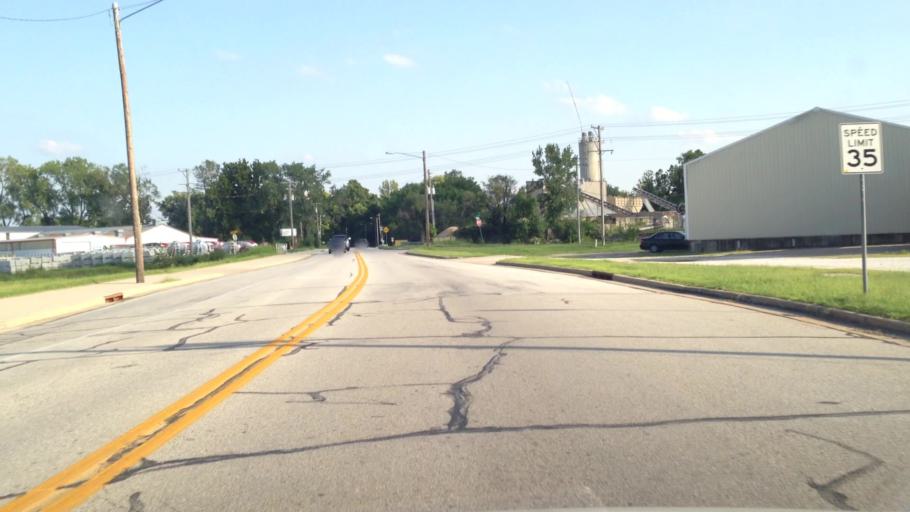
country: US
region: Missouri
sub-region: Jasper County
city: Joplin
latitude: 37.0873
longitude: -94.5069
